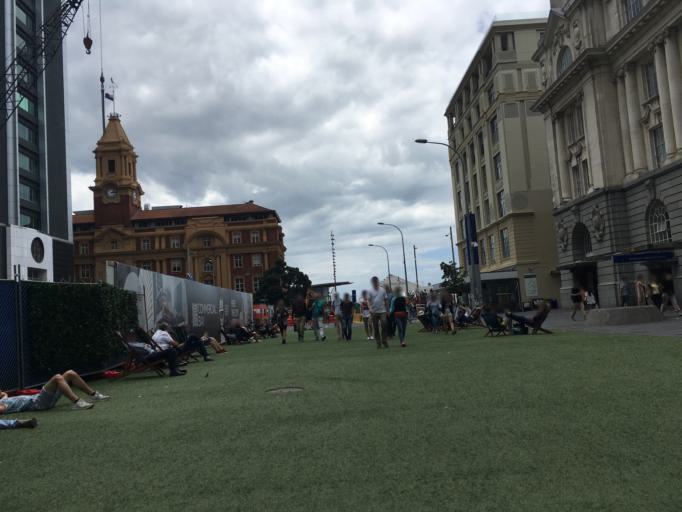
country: NZ
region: Auckland
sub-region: Auckland
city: Auckland
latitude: -36.8441
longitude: 174.7669
